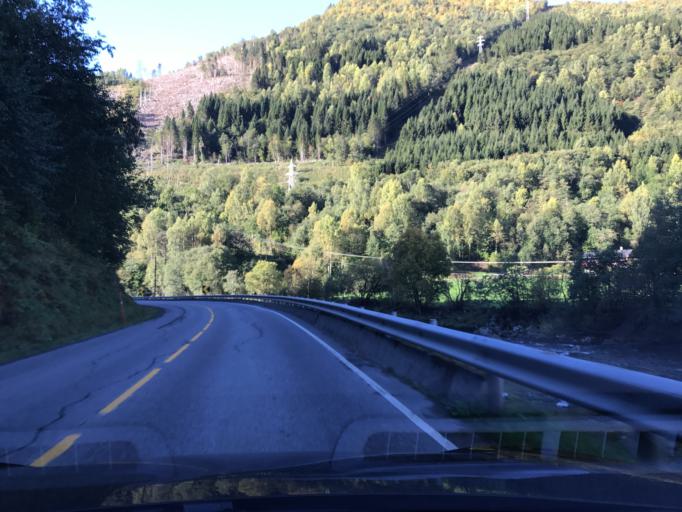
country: NO
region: More og Romsdal
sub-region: Norddal
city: Valldal
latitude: 62.3072
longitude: 7.2559
